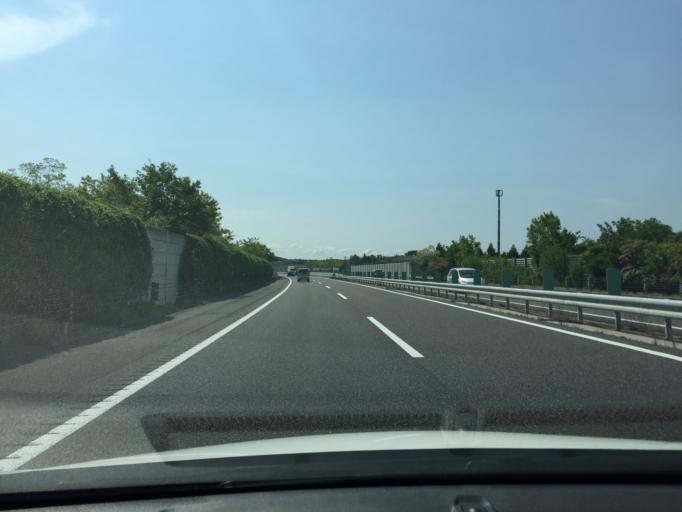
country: JP
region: Fukushima
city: Koriyama
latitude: 37.3612
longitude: 140.3138
